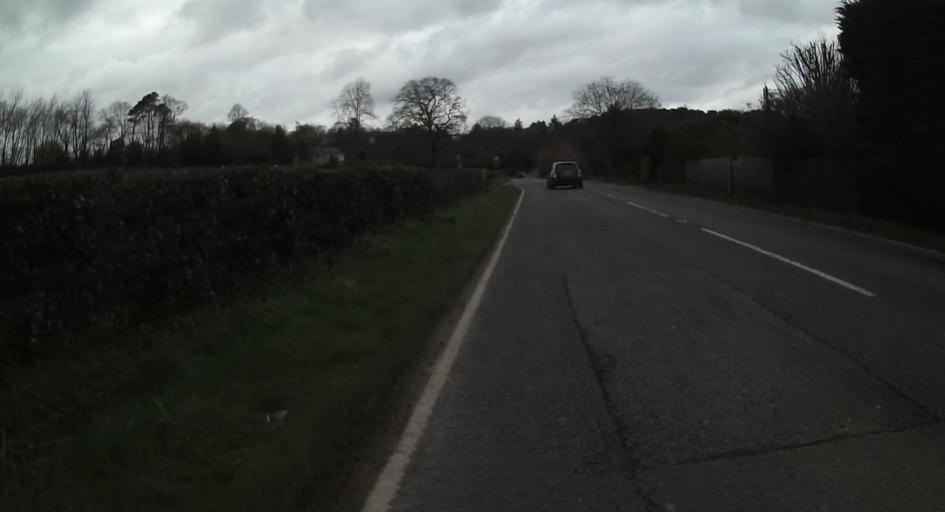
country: GB
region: England
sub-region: Surrey
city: Farnham
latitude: 51.1796
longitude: -0.7912
